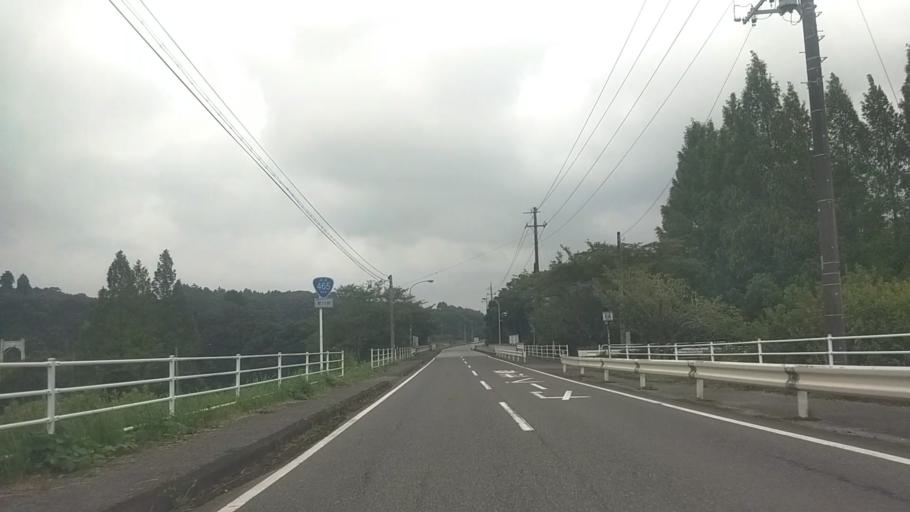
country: JP
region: Chiba
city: Kawaguchi
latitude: 35.2269
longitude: 140.0911
